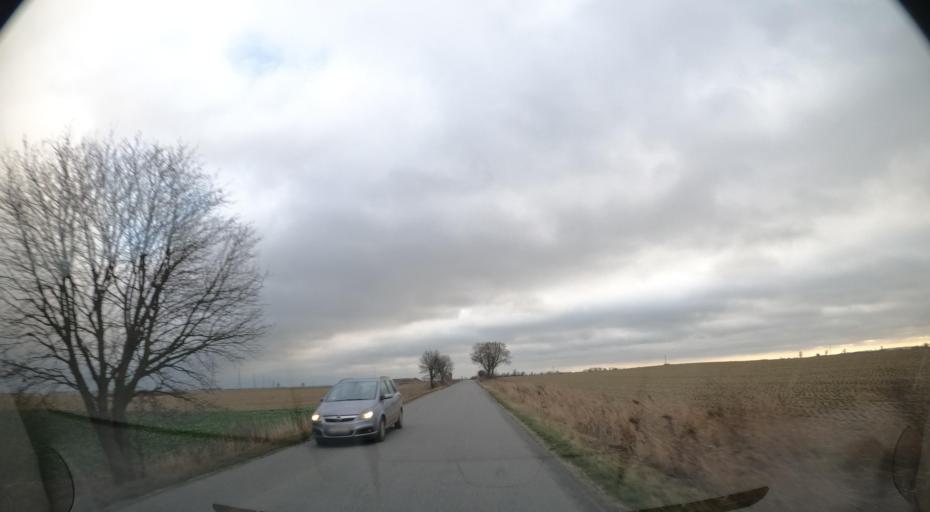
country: PL
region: Kujawsko-Pomorskie
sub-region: Powiat nakielski
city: Sadki
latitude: 53.1748
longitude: 17.4222
